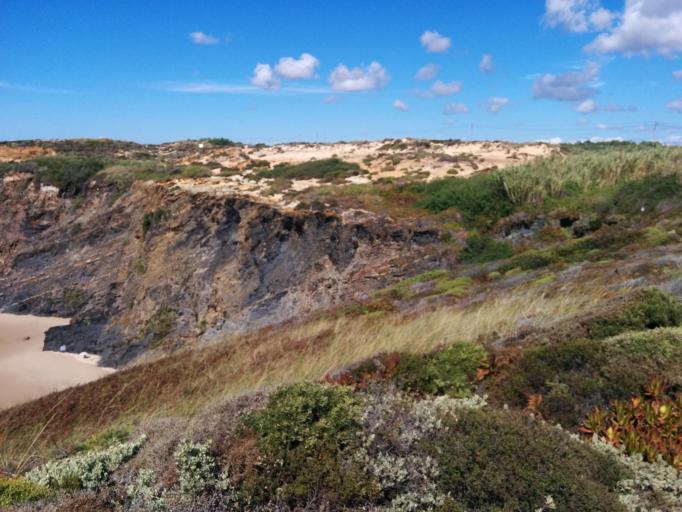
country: PT
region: Beja
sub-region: Odemira
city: Sao Teotonio
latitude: 37.5312
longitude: -8.7859
